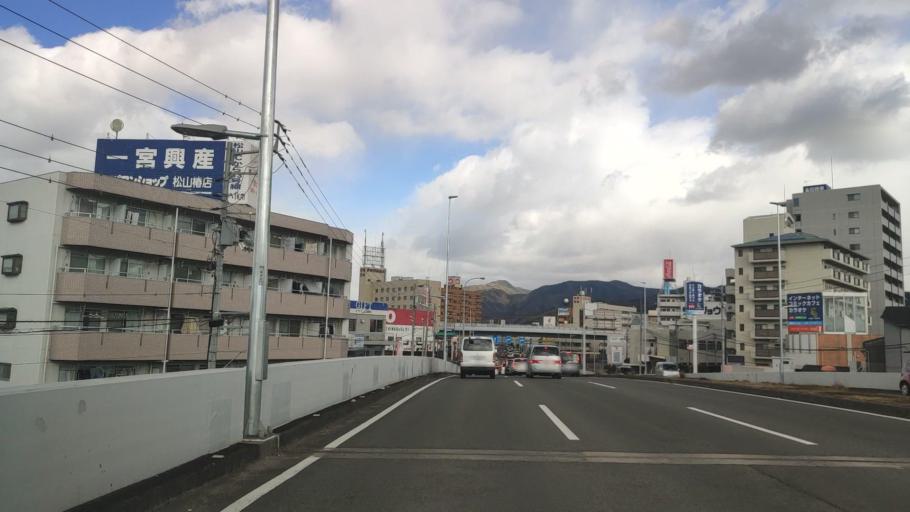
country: JP
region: Ehime
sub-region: Shikoku-chuo Shi
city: Matsuyama
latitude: 33.8253
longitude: 132.7811
